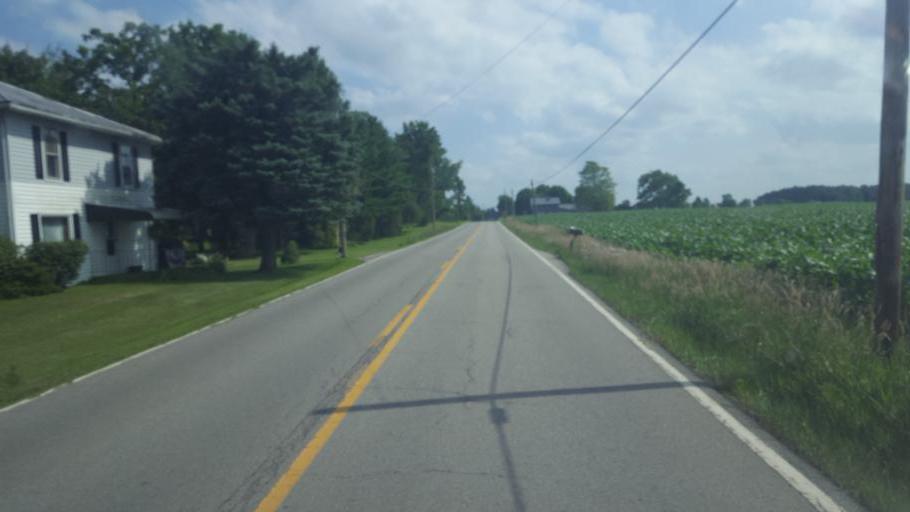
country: US
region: Ohio
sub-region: Richland County
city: Shelby
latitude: 40.9185
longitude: -82.7722
